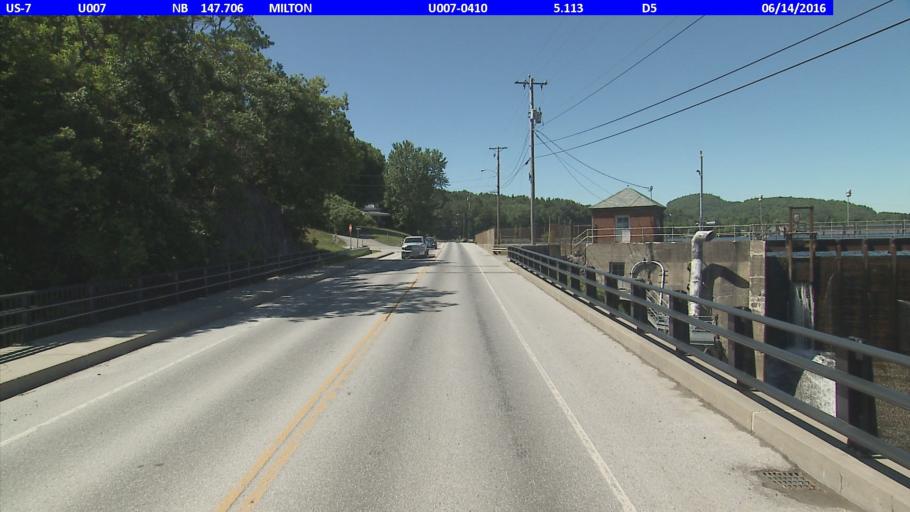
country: US
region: Vermont
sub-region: Chittenden County
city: Milton
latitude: 44.6409
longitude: -73.1139
